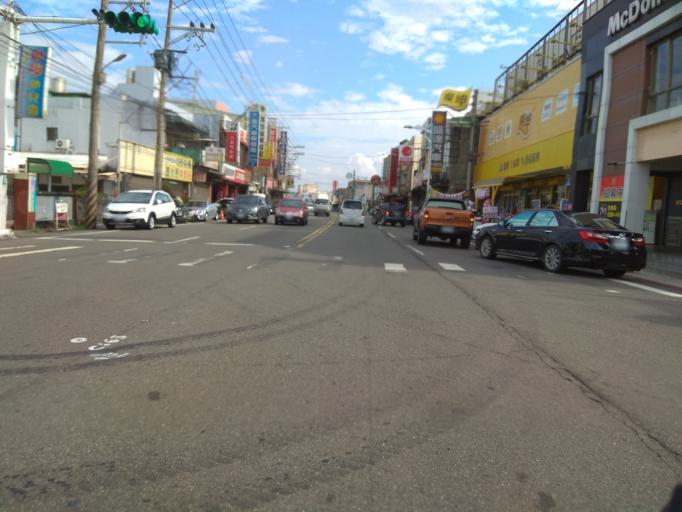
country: TW
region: Taiwan
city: Taoyuan City
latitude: 25.0621
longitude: 121.2021
